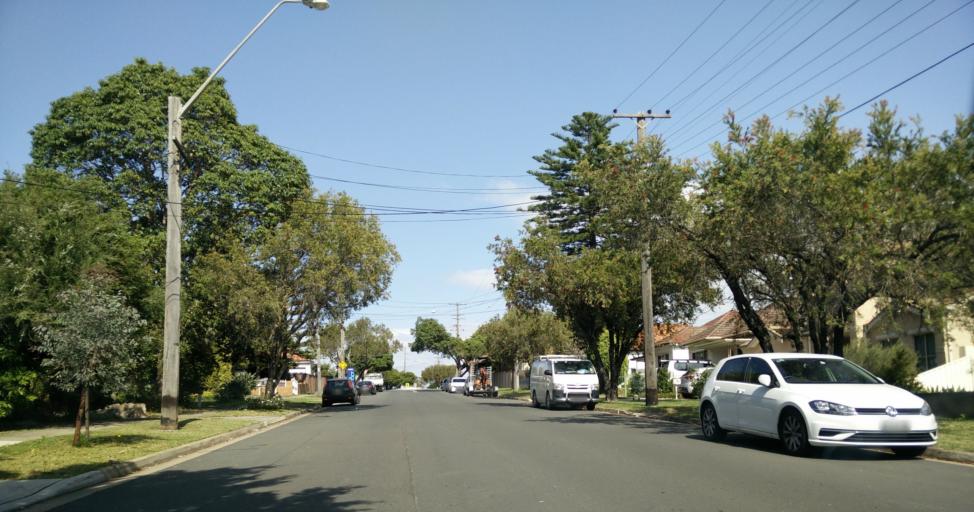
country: AU
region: New South Wales
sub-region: Bankstown
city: Padstow
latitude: -33.9504
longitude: 151.0265
